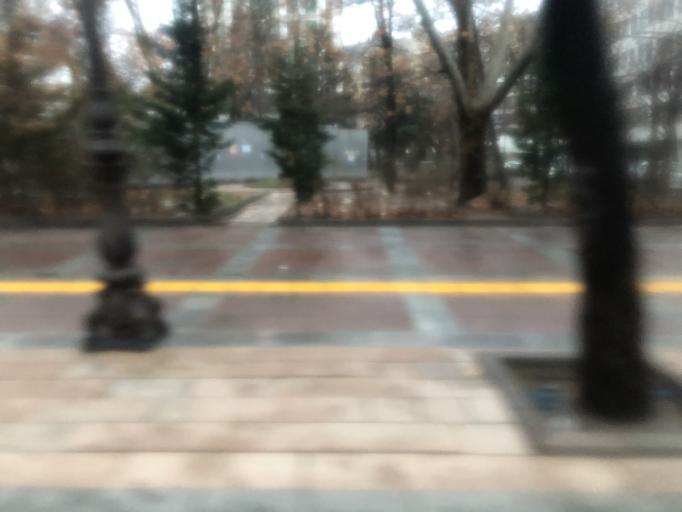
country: TR
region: Ankara
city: Ankara
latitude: 39.9250
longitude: 32.8546
